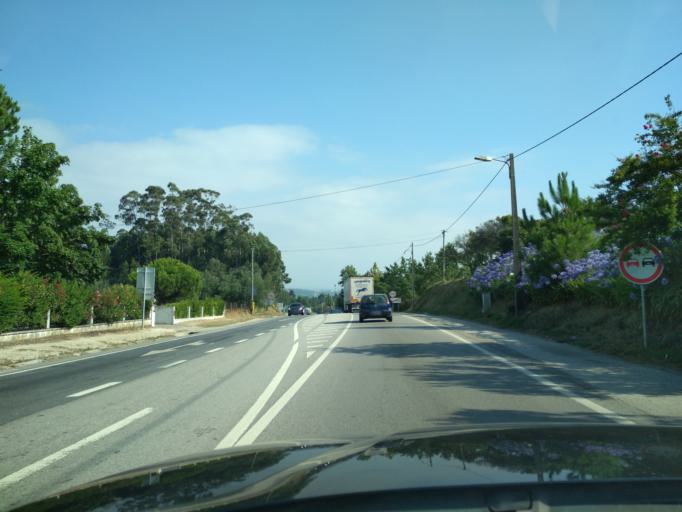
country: PT
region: Aveiro
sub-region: Mealhada
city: Pampilhosa do Botao
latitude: 40.3048
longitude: -8.4483
